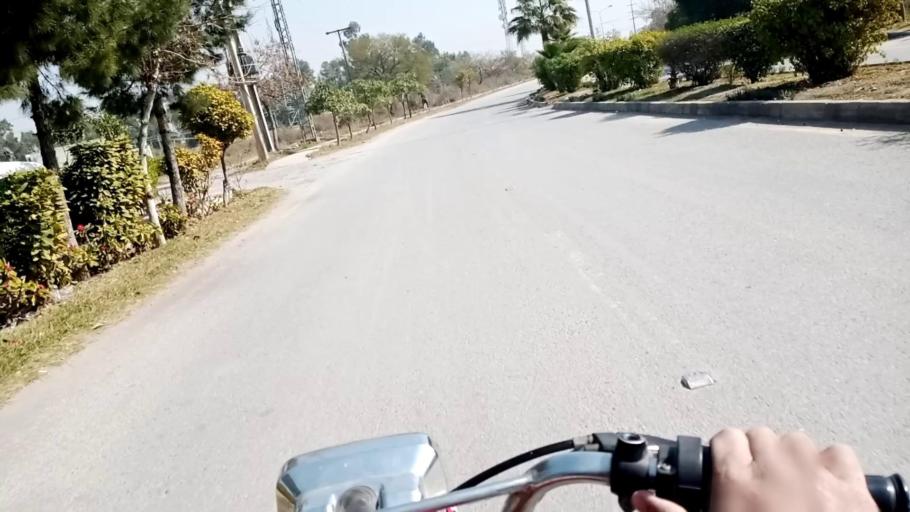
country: PK
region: Khyber Pakhtunkhwa
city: Peshawar
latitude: 33.9640
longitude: 71.4264
